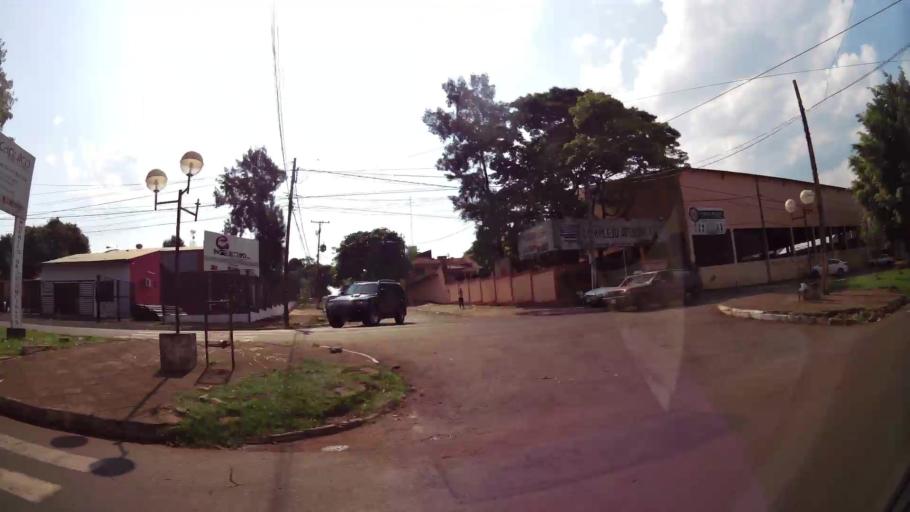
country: PY
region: Alto Parana
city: Ciudad del Este
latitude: -25.5062
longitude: -54.6295
